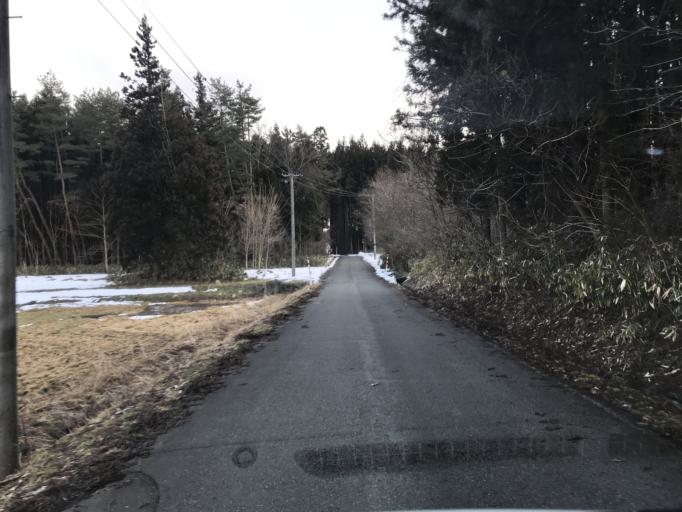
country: JP
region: Iwate
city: Mizusawa
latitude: 39.1086
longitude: 140.9816
